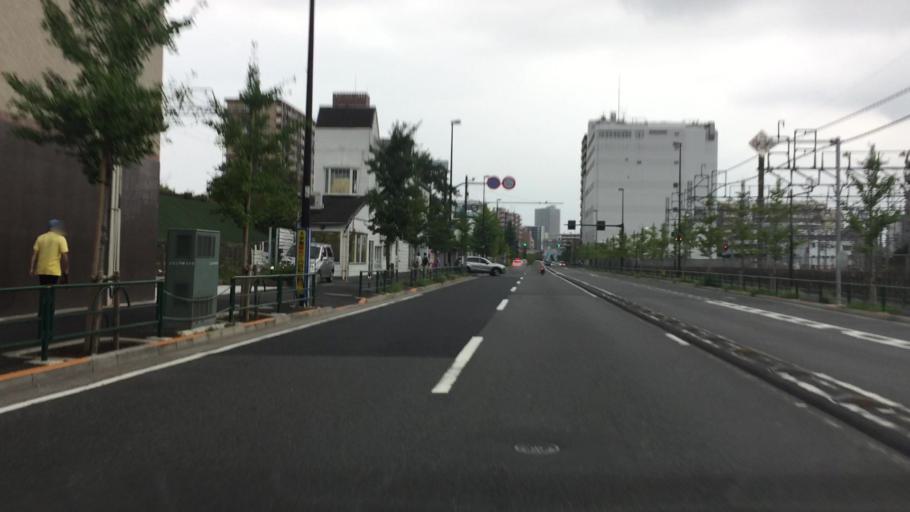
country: JP
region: Saitama
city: Soka
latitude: 35.7441
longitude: 139.8098
